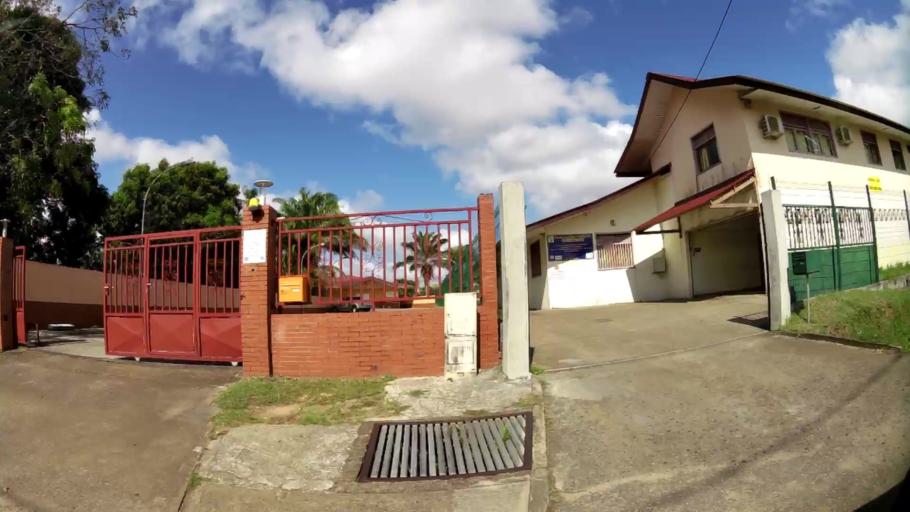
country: GF
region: Guyane
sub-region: Guyane
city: Cayenne
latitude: 4.9354
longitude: -52.3144
